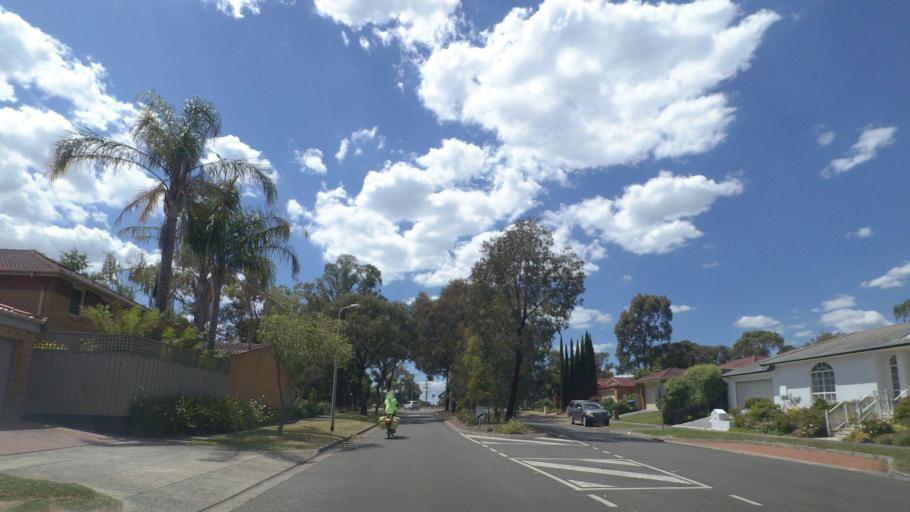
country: AU
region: Victoria
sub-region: Knox
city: Knoxfield
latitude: -37.8752
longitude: 145.2515
